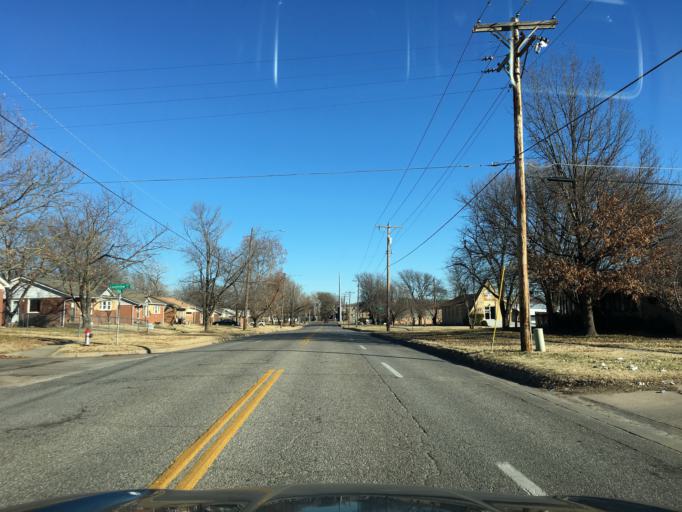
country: US
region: Kansas
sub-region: Sedgwick County
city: Wichita
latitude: 37.6720
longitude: -97.2478
